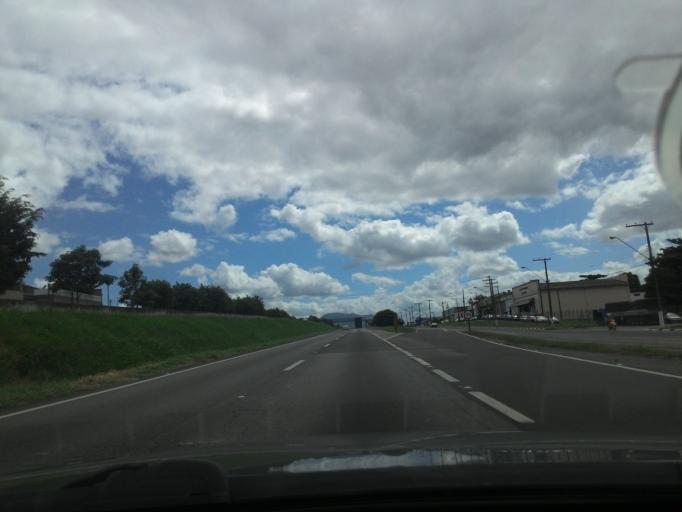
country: BR
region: Sao Paulo
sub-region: Jacupiranga
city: Jacupiranga
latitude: -24.6991
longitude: -48.0044
